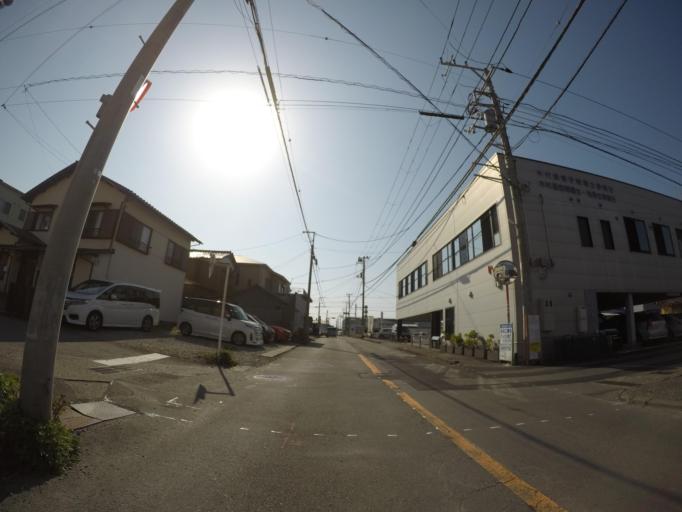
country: JP
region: Shizuoka
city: Numazu
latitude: 35.1033
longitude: 138.8476
